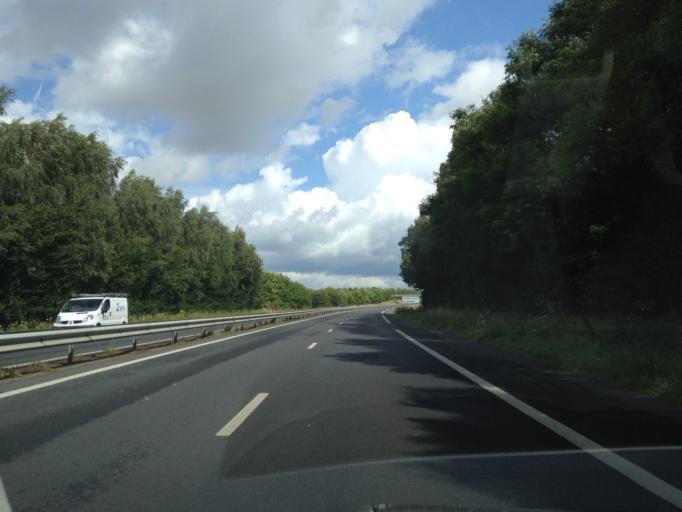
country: FR
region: Haute-Normandie
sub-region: Departement de la Seine-Maritime
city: Saint-Martin-Osmonville
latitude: 49.6248
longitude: 1.2621
